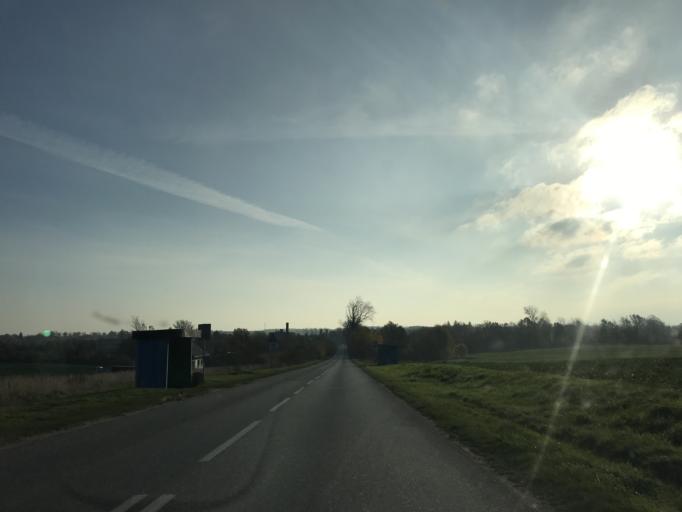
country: PL
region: Pomeranian Voivodeship
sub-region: Powiat pucki
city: Krokowa
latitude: 54.7830
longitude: 18.1514
